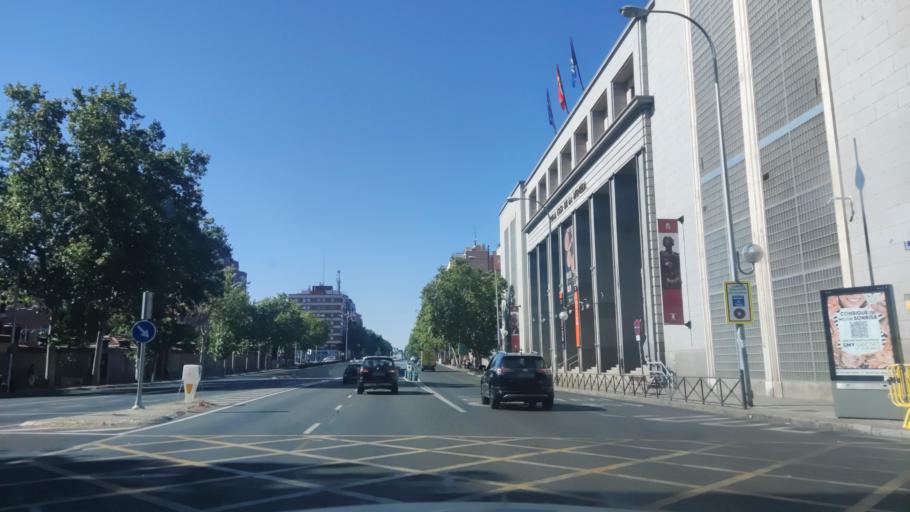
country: ES
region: Madrid
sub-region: Provincia de Madrid
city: Salamanca
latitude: 40.4231
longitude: -3.6689
